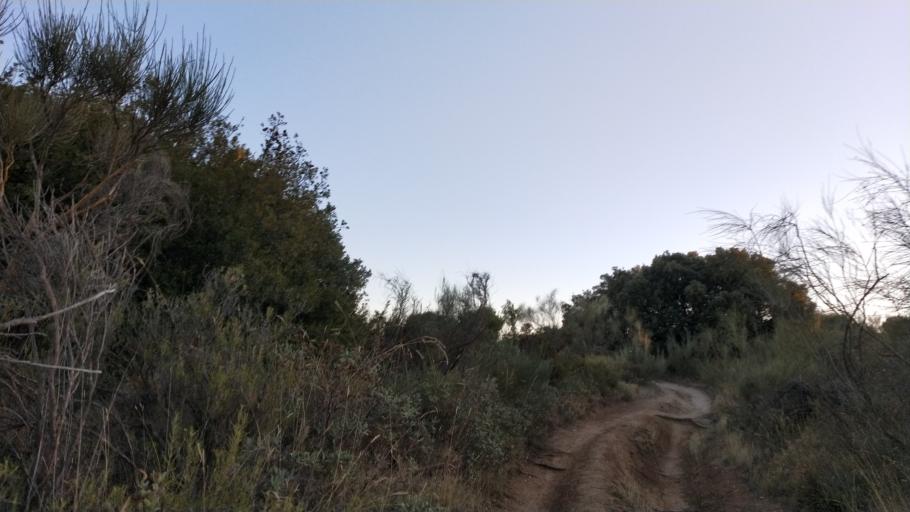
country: ES
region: Andalusia
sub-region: Provincia de Granada
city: Dudar
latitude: 37.2014
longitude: -3.5018
